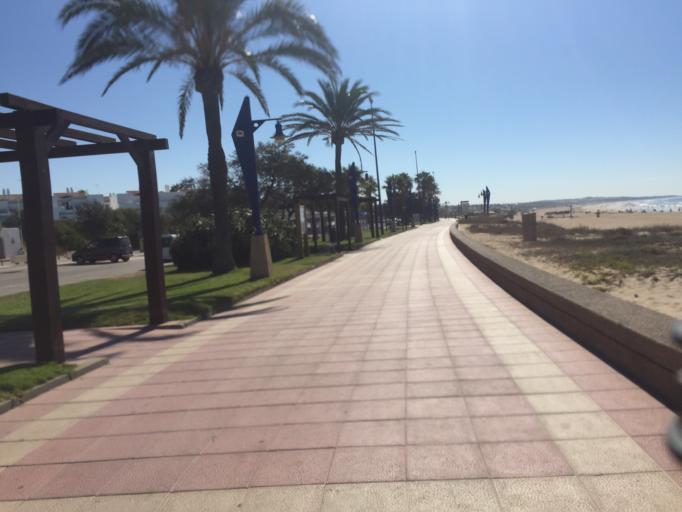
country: ES
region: Andalusia
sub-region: Provincia de Cadiz
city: Chiclana de la Frontera
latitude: 36.3709
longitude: -6.1839
